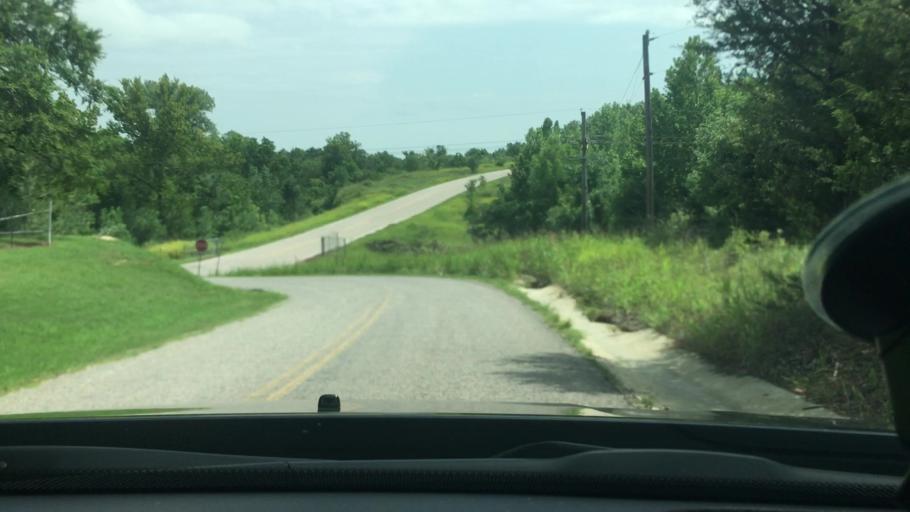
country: US
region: Oklahoma
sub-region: Pontotoc County
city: Ada
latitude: 34.8114
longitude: -96.7094
